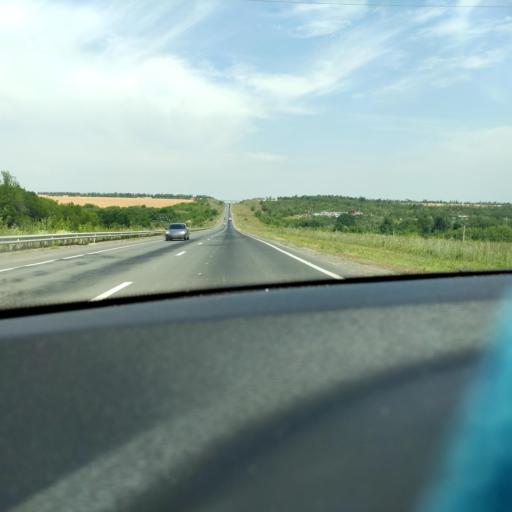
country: RU
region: Samara
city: Petra-Dubrava
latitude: 53.2917
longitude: 50.3871
